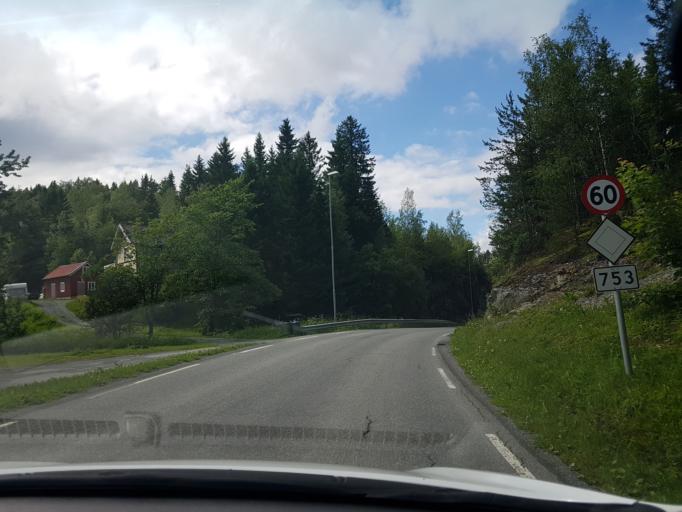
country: NO
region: Nord-Trondelag
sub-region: Stjordal
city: Stjordalshalsen
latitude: 63.6011
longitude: 10.9727
